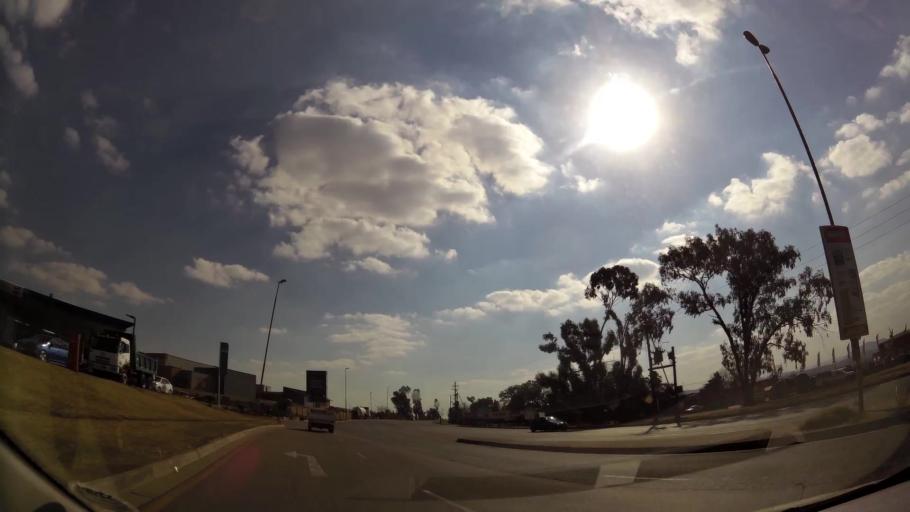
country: ZA
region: Gauteng
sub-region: West Rand District Municipality
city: Muldersdriseloop
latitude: -26.0612
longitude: 27.8318
